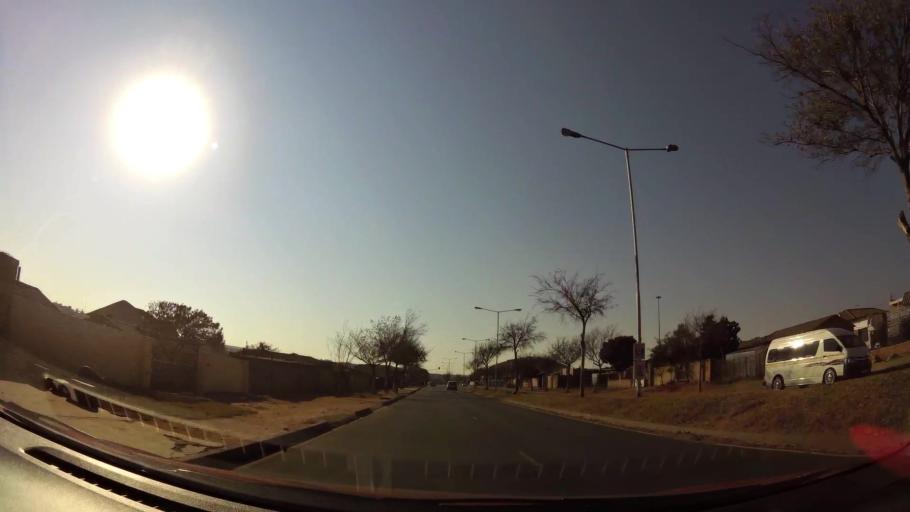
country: ZA
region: Gauteng
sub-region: City of Johannesburg Metropolitan Municipality
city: Soweto
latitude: -26.2563
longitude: 27.9374
